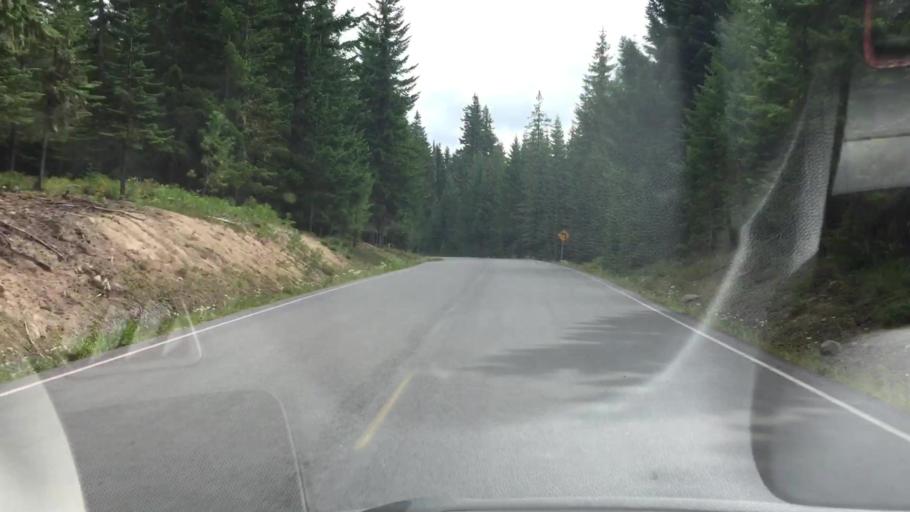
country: US
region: Washington
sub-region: Klickitat County
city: White Salmon
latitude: 46.1907
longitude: -121.6495
